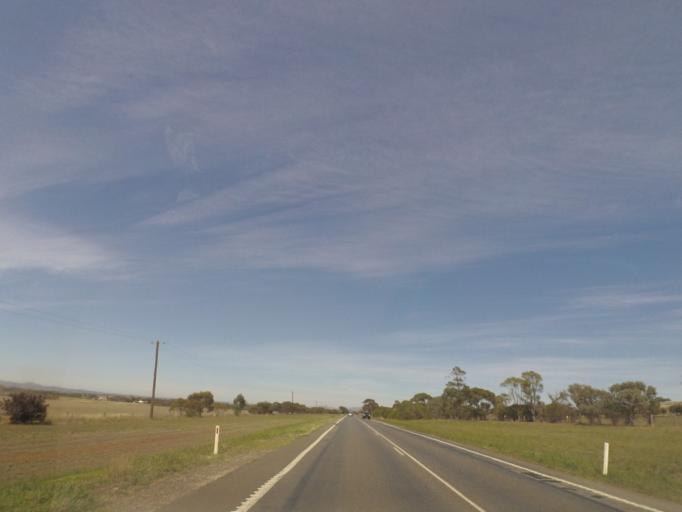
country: AU
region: Victoria
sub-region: Moorabool
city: Bacchus Marsh
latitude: -37.7786
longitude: 144.4341
